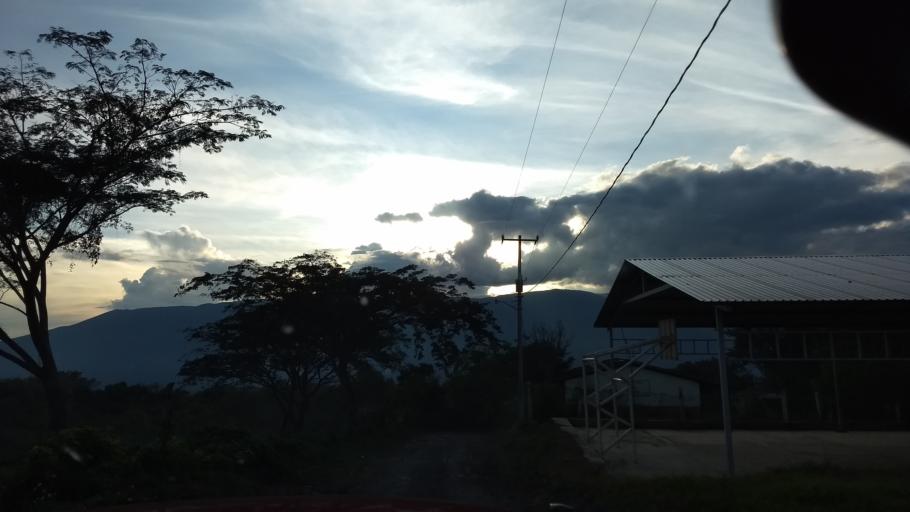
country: MX
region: Jalisco
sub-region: San Gabriel
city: Alista
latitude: 19.5016
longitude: -103.7645
